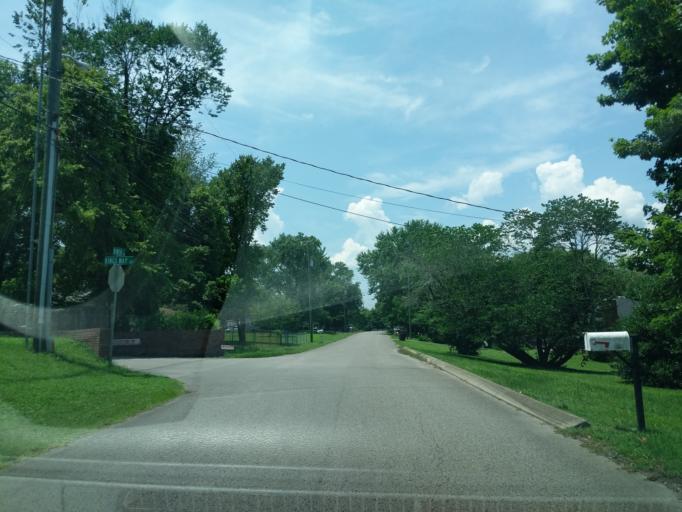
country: US
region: Tennessee
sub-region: Davidson County
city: Lakewood
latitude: 36.2387
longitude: -86.6382
